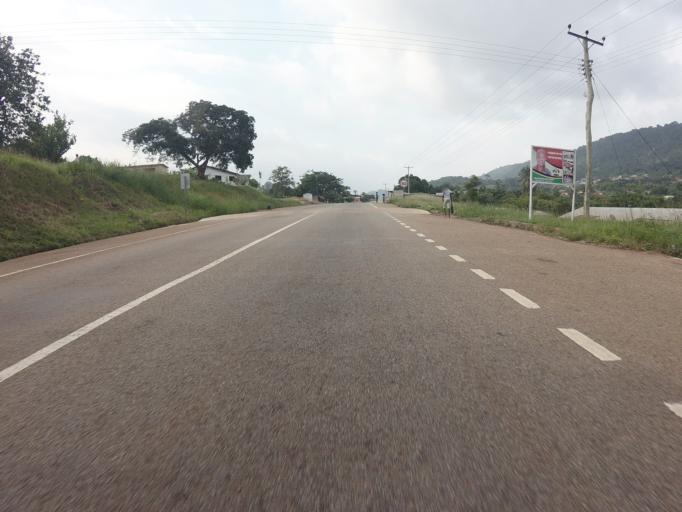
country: GH
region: Volta
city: Ho
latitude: 6.6642
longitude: 0.4734
